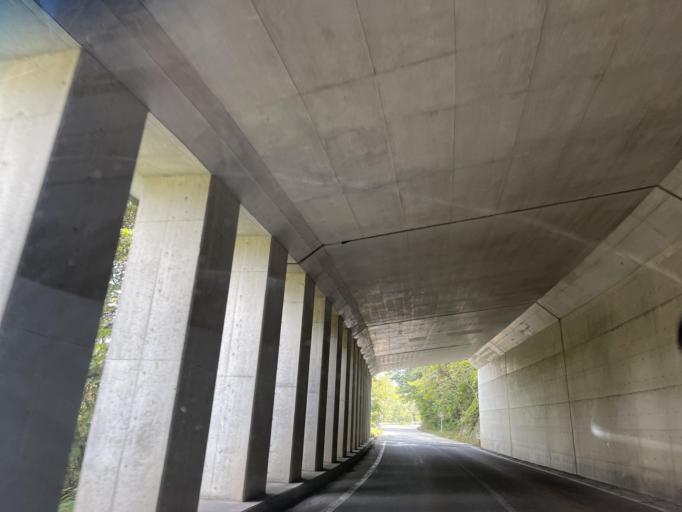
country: JP
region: Nagano
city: Omachi
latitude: 36.5259
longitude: 137.7900
